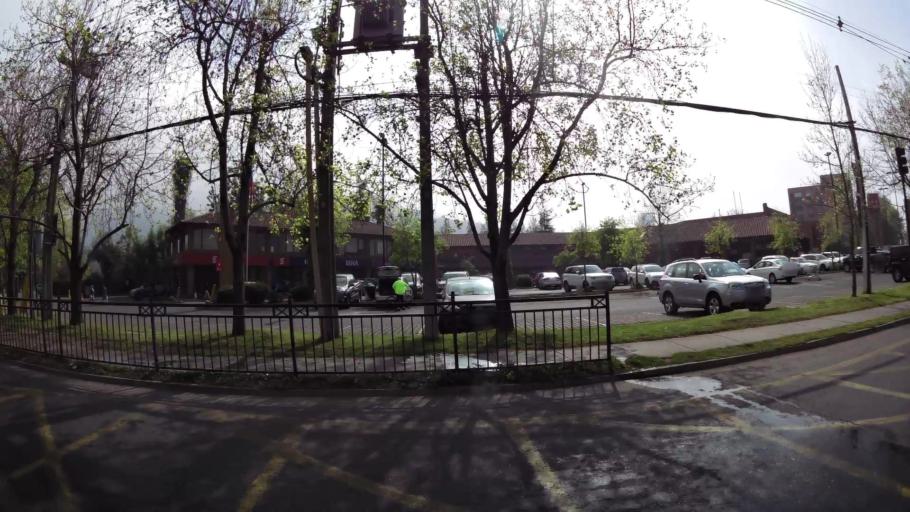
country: CL
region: Santiago Metropolitan
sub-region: Provincia de Santiago
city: Villa Presidente Frei, Nunoa, Santiago, Chile
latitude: -33.3768
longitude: -70.5696
